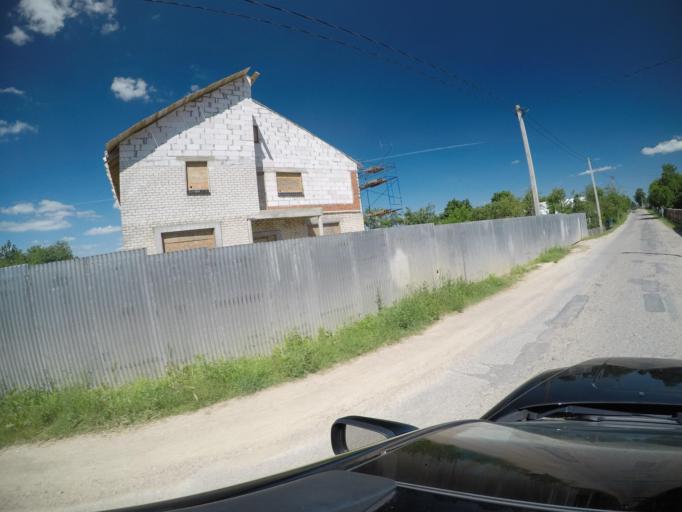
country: BY
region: Grodnenskaya
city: Hrodna
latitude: 53.7225
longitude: 23.8479
